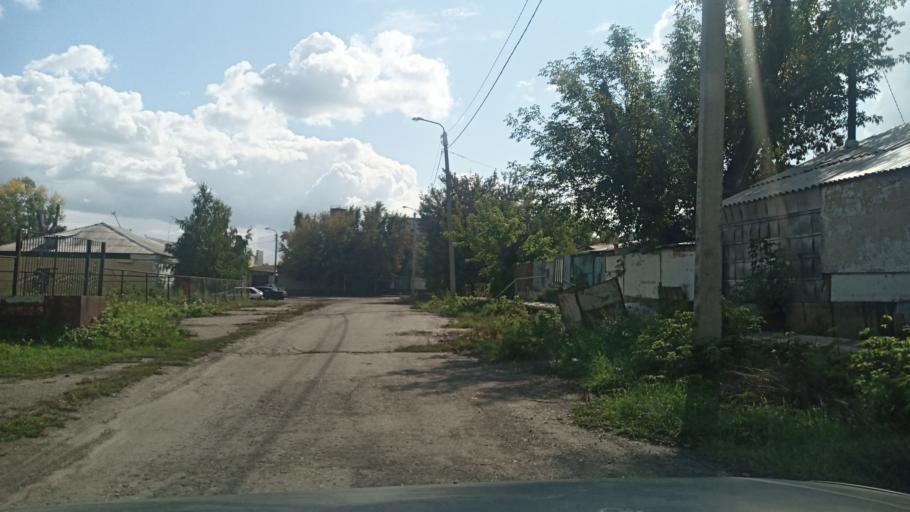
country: RU
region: Altai Krai
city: Zaton
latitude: 53.2983
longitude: 83.8011
